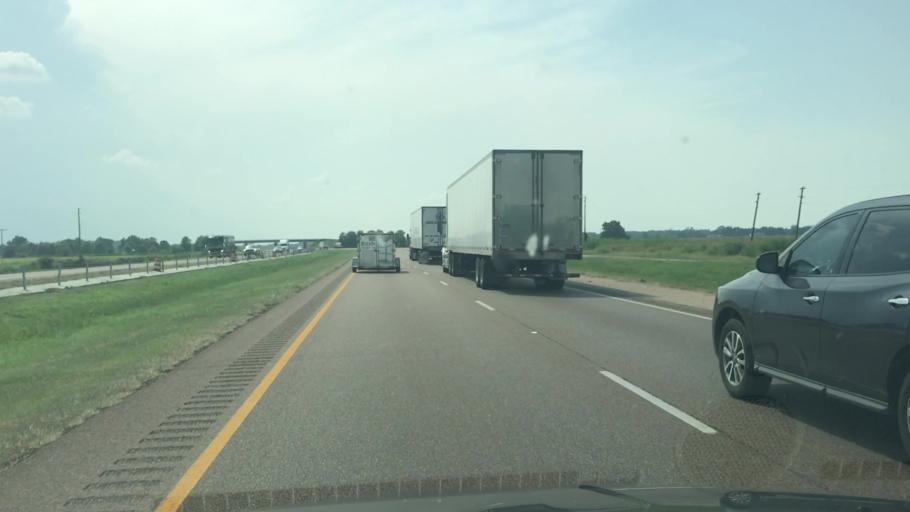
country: US
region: Arkansas
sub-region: Crittenden County
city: Earle
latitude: 35.1514
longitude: -90.3935
